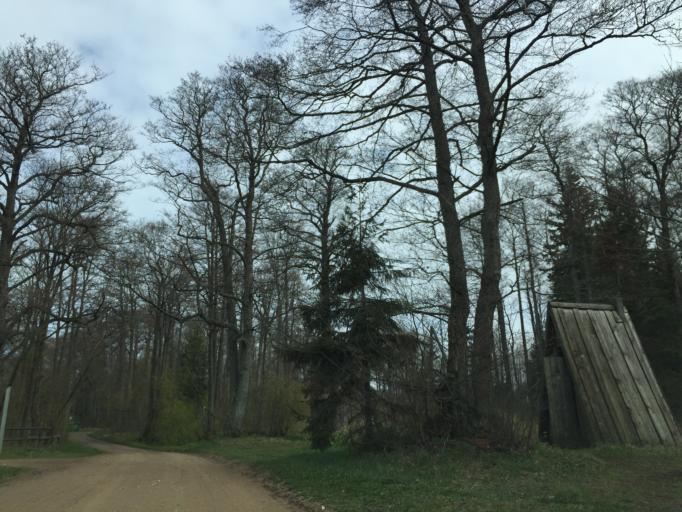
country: LV
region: Salacgrivas
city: Salacgriva
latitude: 57.5205
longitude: 24.3793
